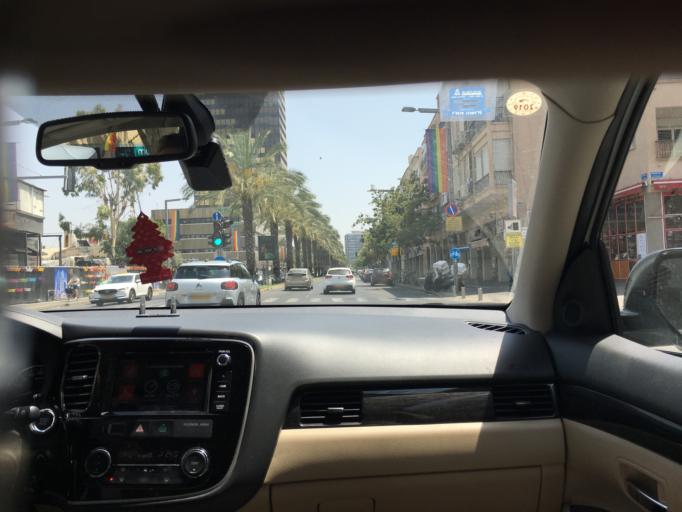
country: IL
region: Tel Aviv
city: Tel Aviv
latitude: 32.0883
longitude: 34.7822
